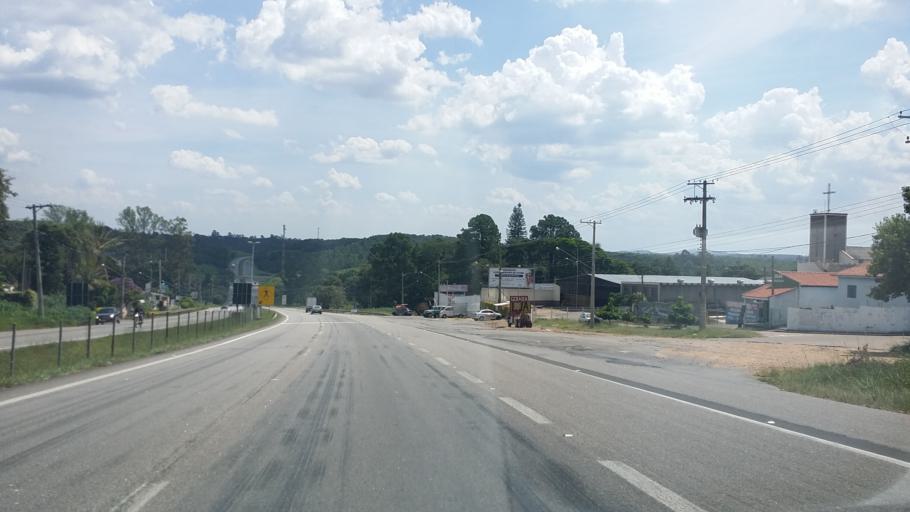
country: BR
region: Sao Paulo
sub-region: Itupeva
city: Itupeva
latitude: -23.1904
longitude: -46.9885
